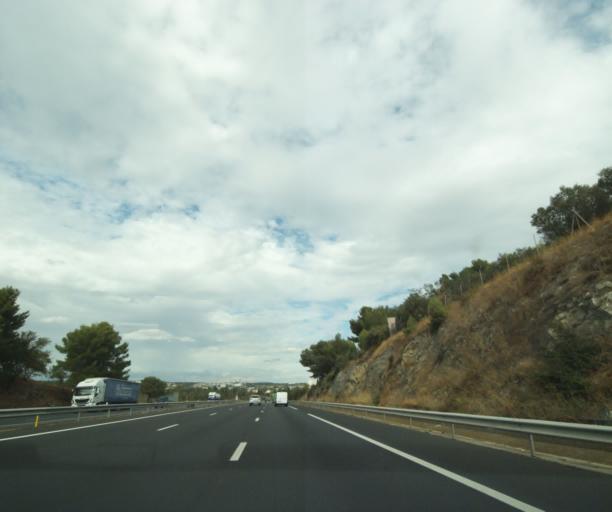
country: FR
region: Languedoc-Roussillon
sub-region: Departement du Gard
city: Milhaud
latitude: 43.7958
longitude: 4.3065
